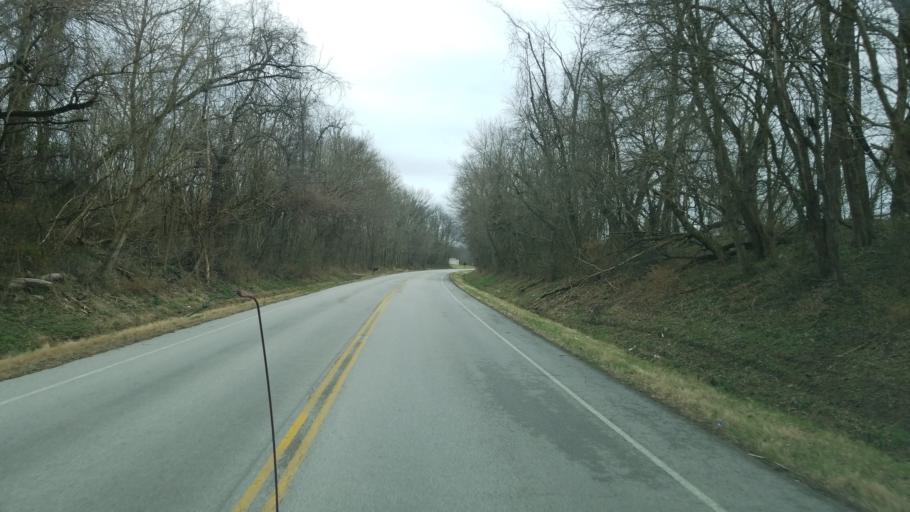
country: US
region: Kentucky
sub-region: Bracken County
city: Augusta
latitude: 38.7887
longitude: -83.9410
